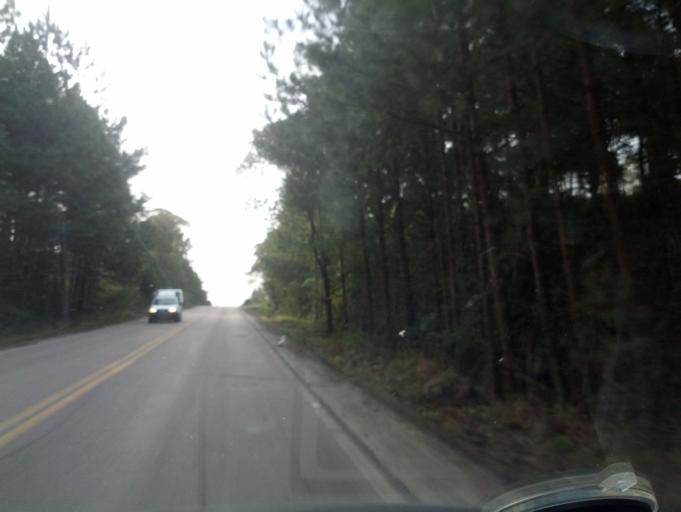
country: BR
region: Santa Catarina
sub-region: Otacilio Costa
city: Otacilio Costa
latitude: -27.3380
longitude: -50.1316
